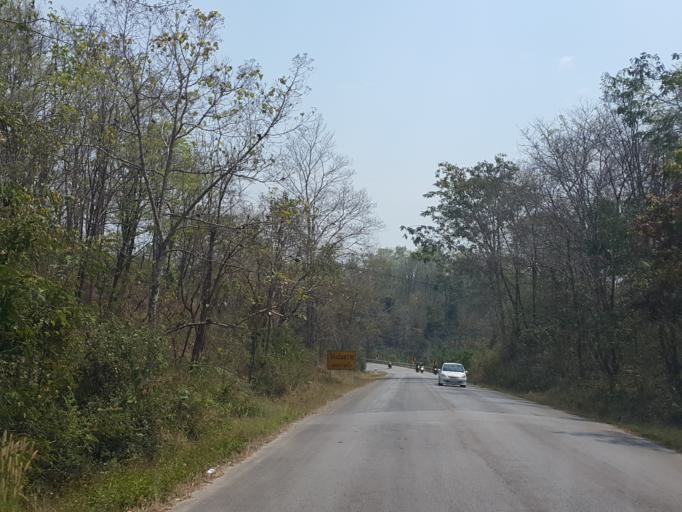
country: TH
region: Lampang
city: Mueang Pan
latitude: 18.7759
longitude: 99.5435
